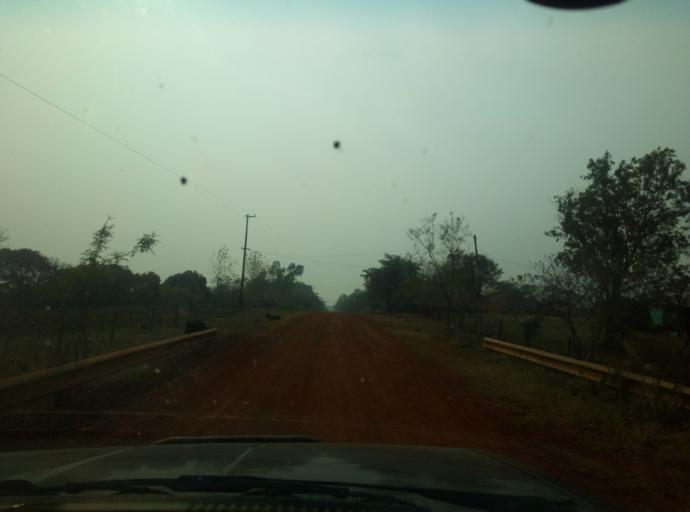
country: PY
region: Caaguazu
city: Carayao
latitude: -25.2043
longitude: -56.2499
